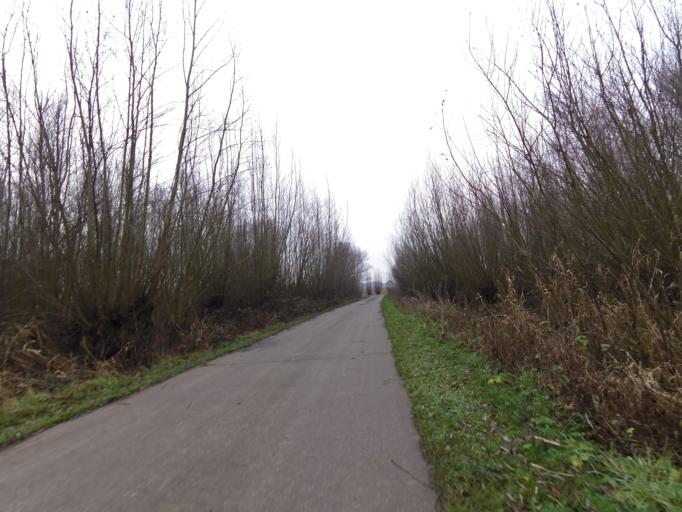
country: NL
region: South Holland
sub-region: Gemeente Oud-Beijerland
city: Oud-Beijerland
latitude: 51.8390
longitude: 4.3932
